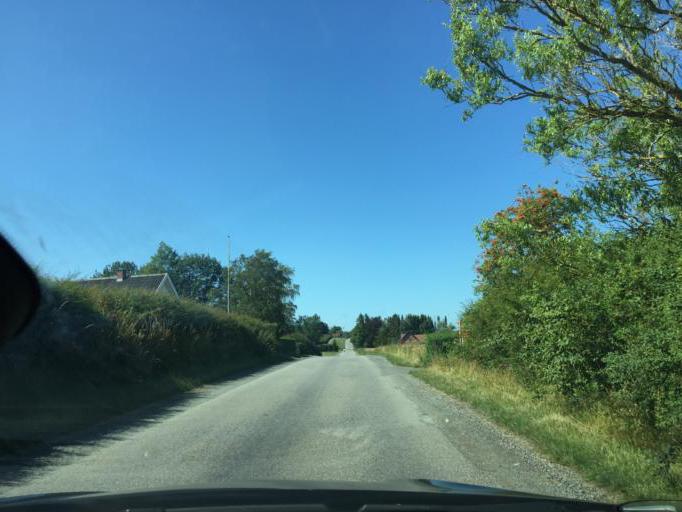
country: DK
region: South Denmark
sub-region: Nordfyns Kommune
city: Sonderso
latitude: 55.4806
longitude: 10.2660
